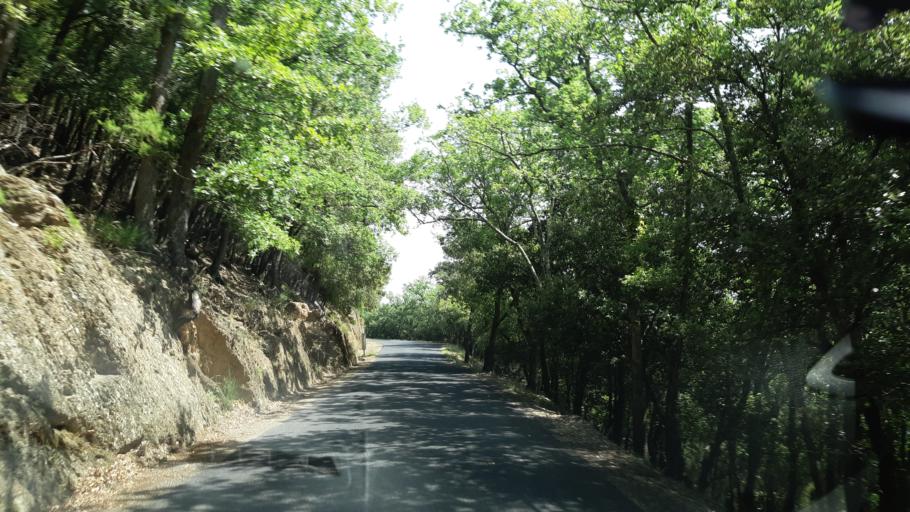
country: FR
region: Languedoc-Roussillon
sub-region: Departement des Pyrenees-Orientales
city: els Banys d'Arles
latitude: 42.5106
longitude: 2.6371
